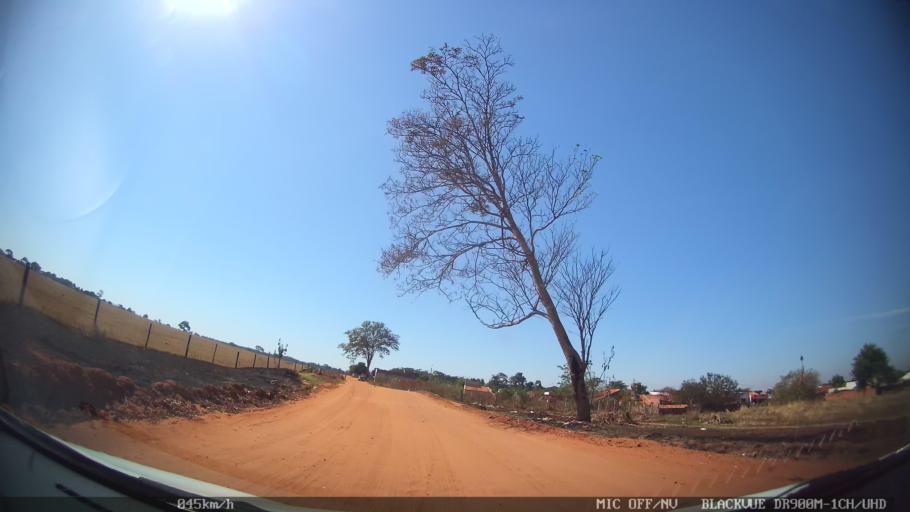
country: BR
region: Sao Paulo
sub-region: Sao Jose Do Rio Preto
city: Sao Jose do Rio Preto
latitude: -20.7444
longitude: -49.4330
